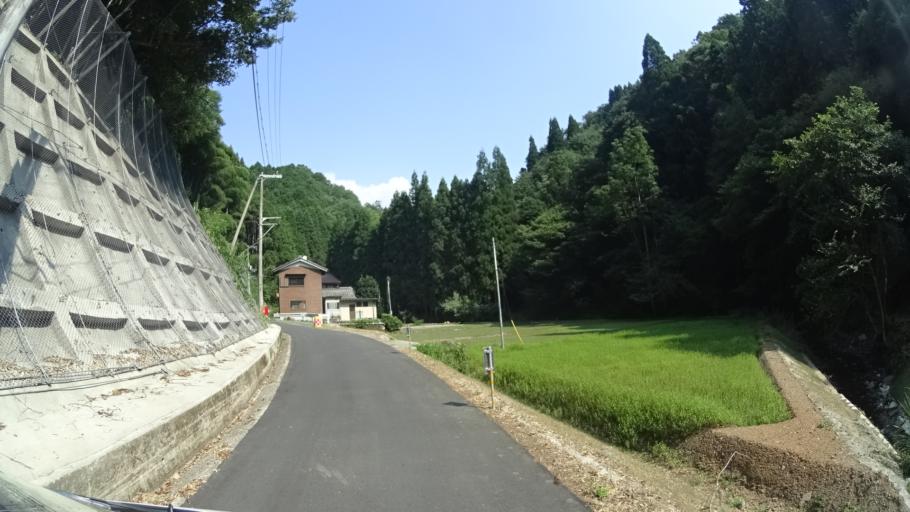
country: JP
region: Kyoto
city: Maizuru
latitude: 35.4091
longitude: 135.2323
